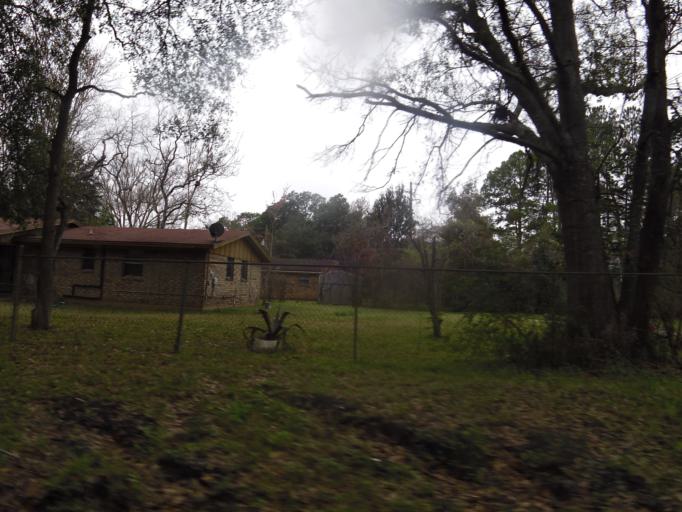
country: US
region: Florida
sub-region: Duval County
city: Jacksonville
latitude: 30.3634
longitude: -81.7036
